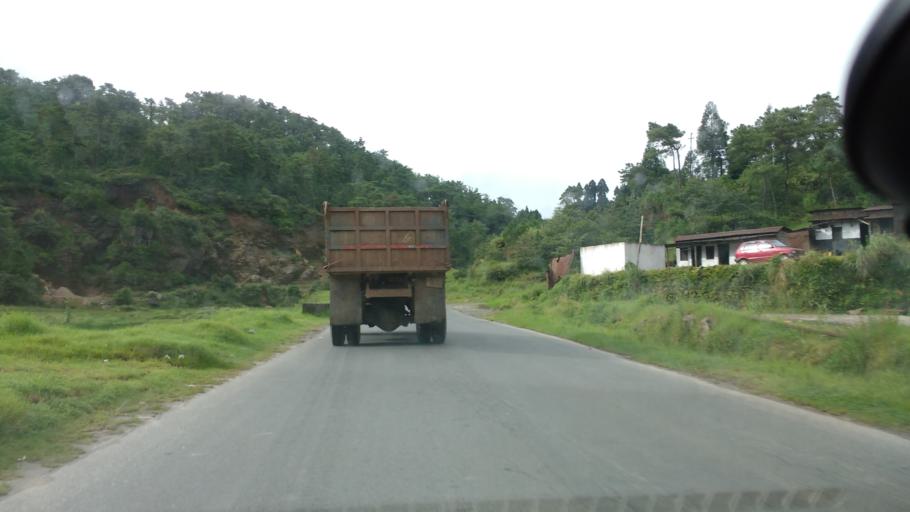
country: IN
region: Meghalaya
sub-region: East Khasi Hills
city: Shillong
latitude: 25.4787
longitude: 91.8202
